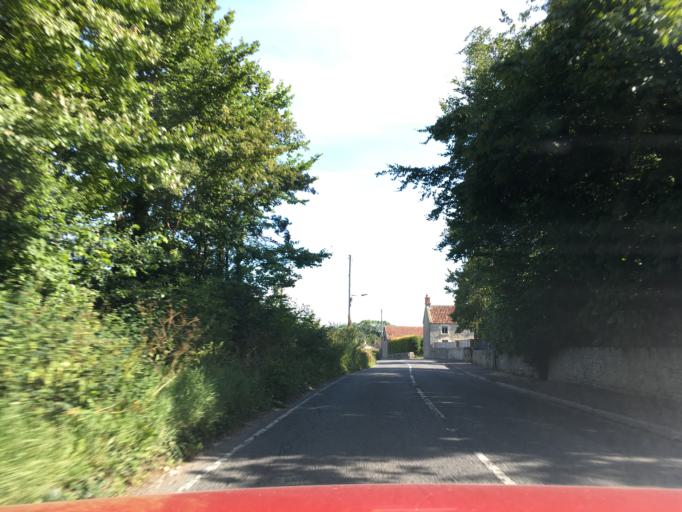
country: GB
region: England
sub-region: South Gloucestershire
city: Pucklechurch
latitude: 51.4504
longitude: -2.4178
